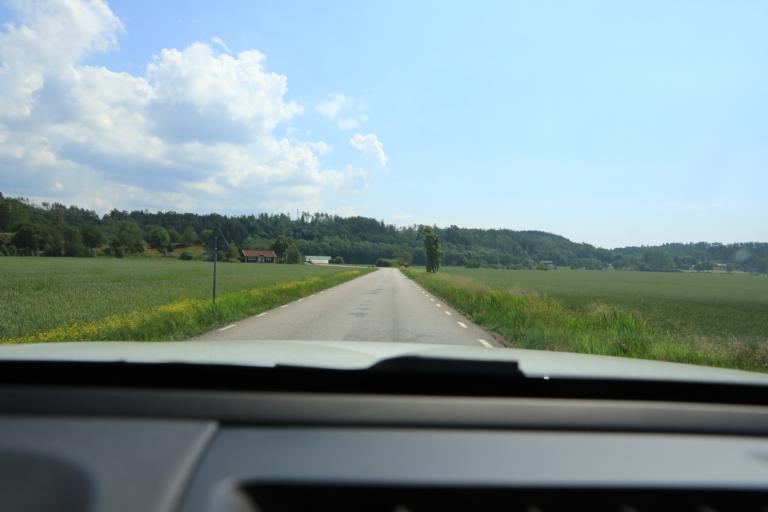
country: SE
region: Halland
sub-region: Varbergs Kommun
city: Veddige
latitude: 57.2056
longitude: 12.3226
